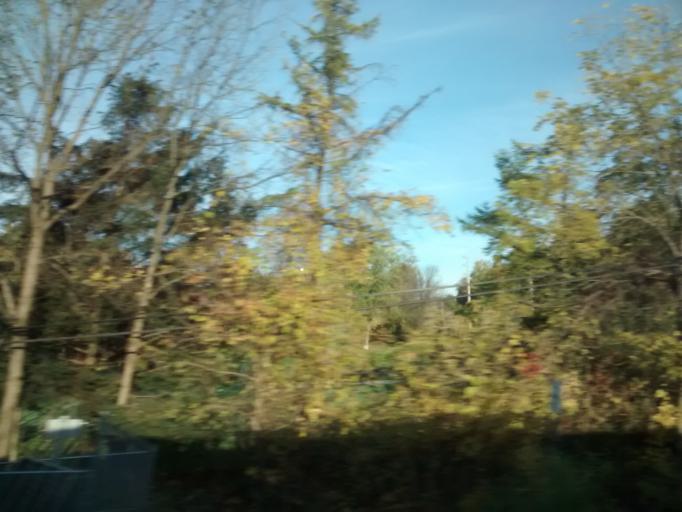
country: CA
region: Ontario
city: Etobicoke
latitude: 43.5862
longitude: -79.5541
